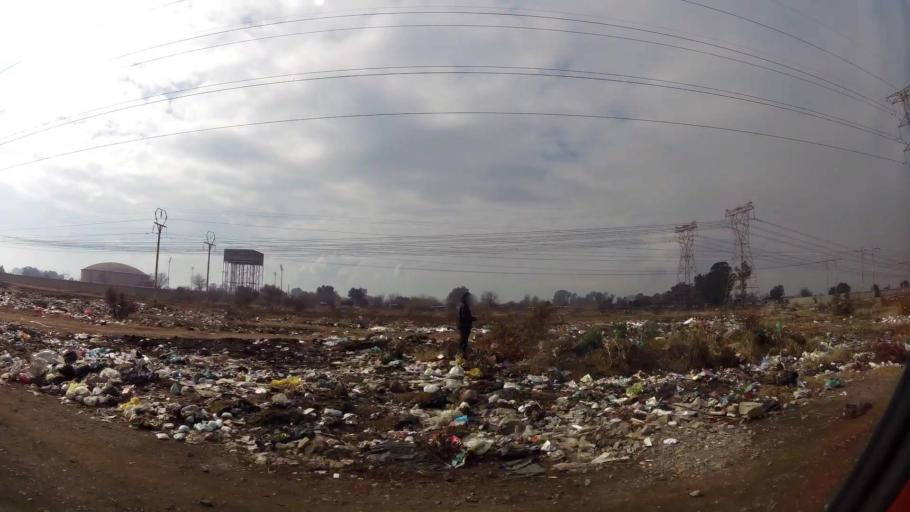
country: ZA
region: Gauteng
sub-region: Sedibeng District Municipality
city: Vanderbijlpark
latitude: -26.6894
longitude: 27.8605
